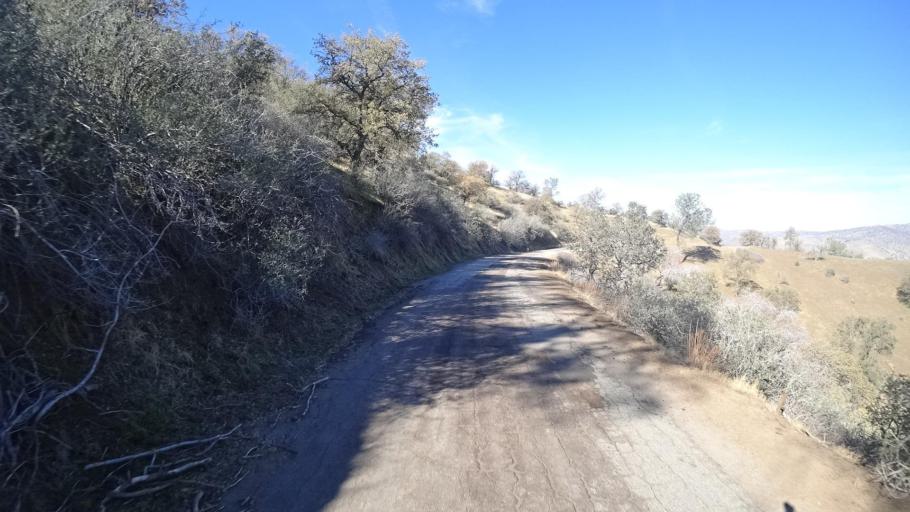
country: US
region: California
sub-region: Kern County
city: Bodfish
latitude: 35.4415
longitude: -118.7055
